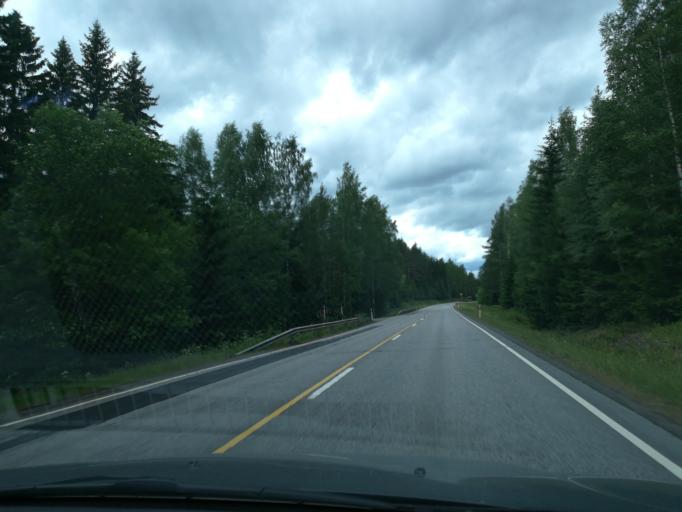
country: FI
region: South Karelia
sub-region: Lappeenranta
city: Lemi
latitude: 61.1258
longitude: 27.8393
